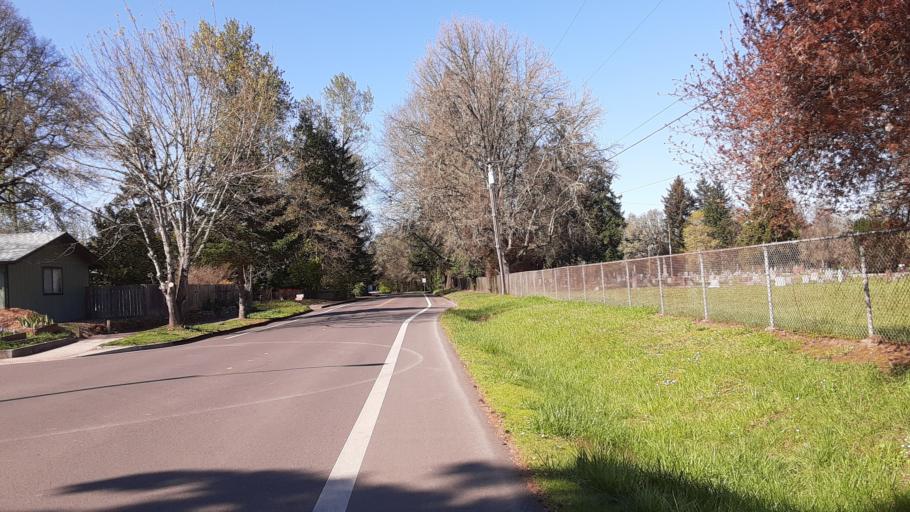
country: US
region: Oregon
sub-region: Benton County
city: Corvallis
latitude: 44.5475
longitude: -123.2557
